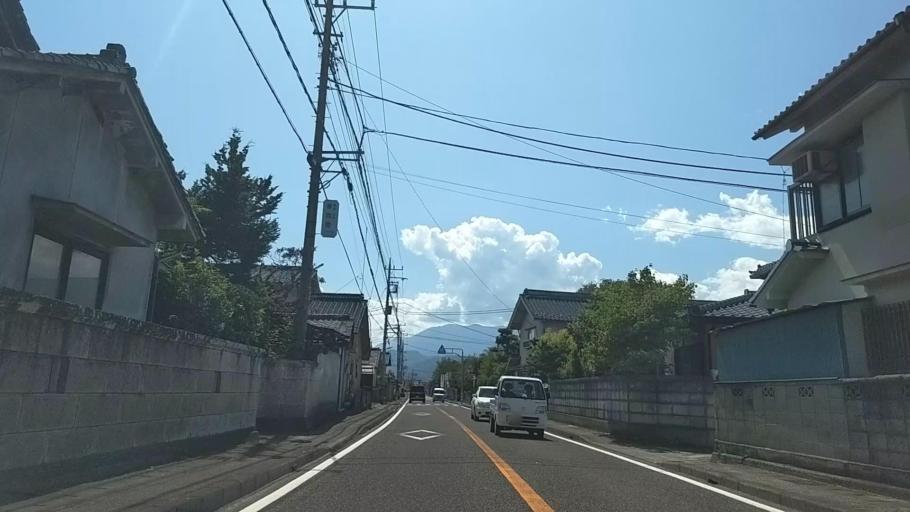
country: JP
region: Yamanashi
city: Ryuo
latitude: 35.5782
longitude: 138.4905
